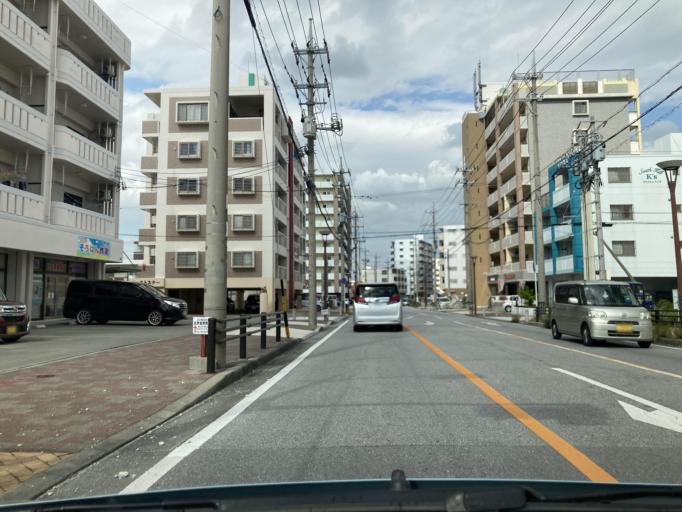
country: JP
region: Okinawa
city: Ginowan
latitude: 26.2502
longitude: 127.7739
